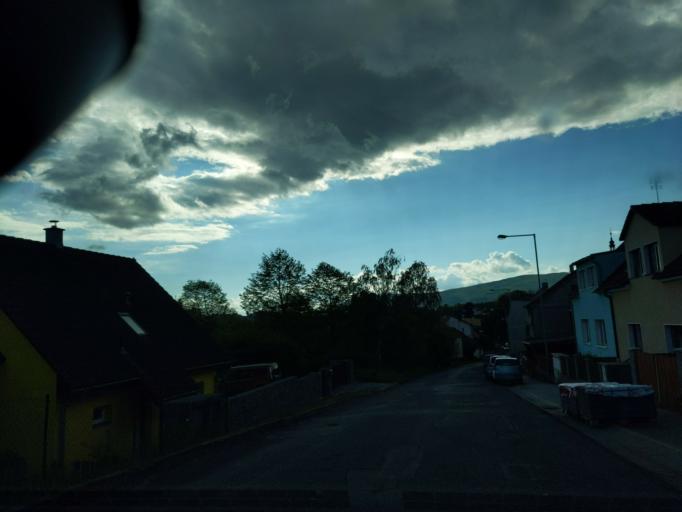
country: CZ
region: Ustecky
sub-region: Okres Usti nad Labem
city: Usti nad Labem
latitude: 50.6883
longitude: 14.0106
